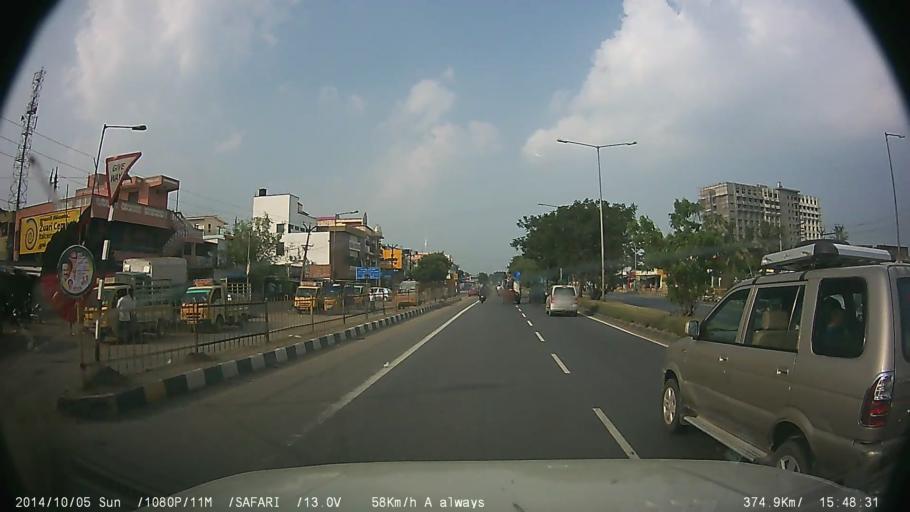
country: IN
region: Tamil Nadu
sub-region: Kancheepuram
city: Singapperumalkovil
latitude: 12.7629
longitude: 80.0040
